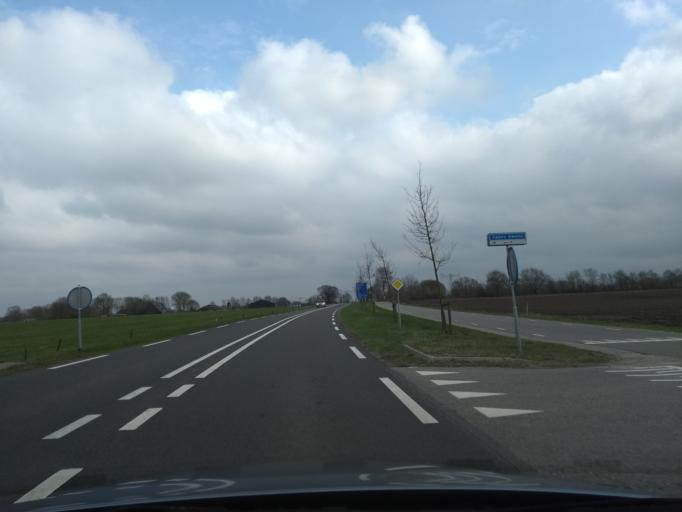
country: NL
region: Overijssel
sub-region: Gemeente Steenwijkerland
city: Sint Jansklooster
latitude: 52.6653
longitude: 5.9868
